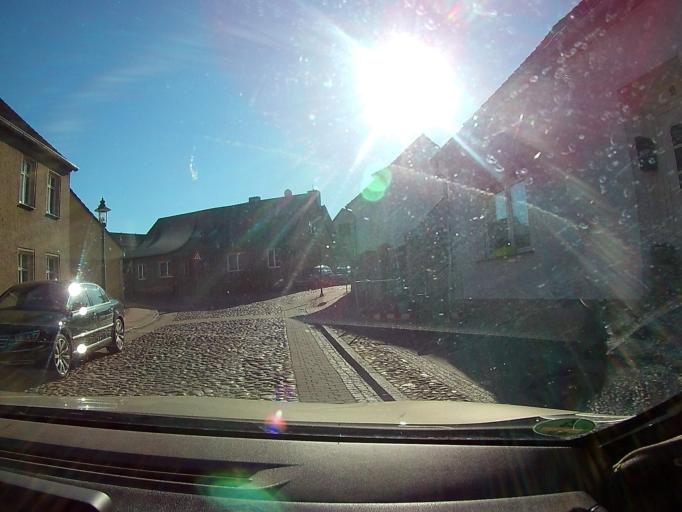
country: DE
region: Brandenburg
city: Rheinsberg
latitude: 53.1572
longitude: 12.7676
